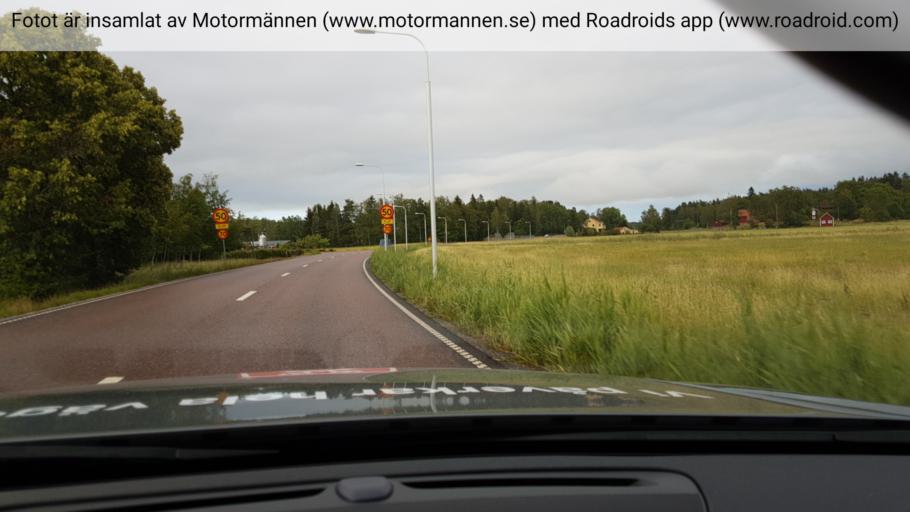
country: SE
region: Soedermanland
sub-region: Eskilstuna Kommun
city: Hallbybrunn
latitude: 59.3196
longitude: 16.3129
